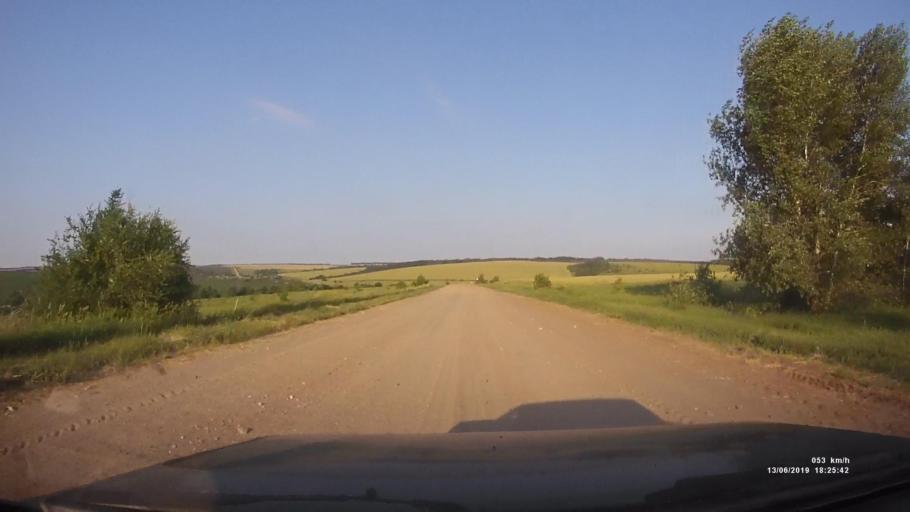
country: RU
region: Rostov
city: Kazanskaya
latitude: 49.8513
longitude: 41.3064
